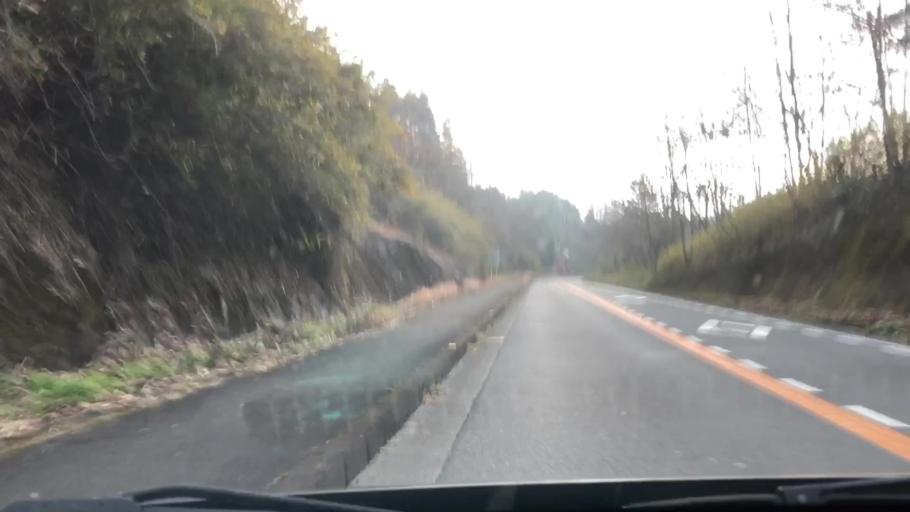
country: JP
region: Oita
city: Takedamachi
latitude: 32.9717
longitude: 131.5037
